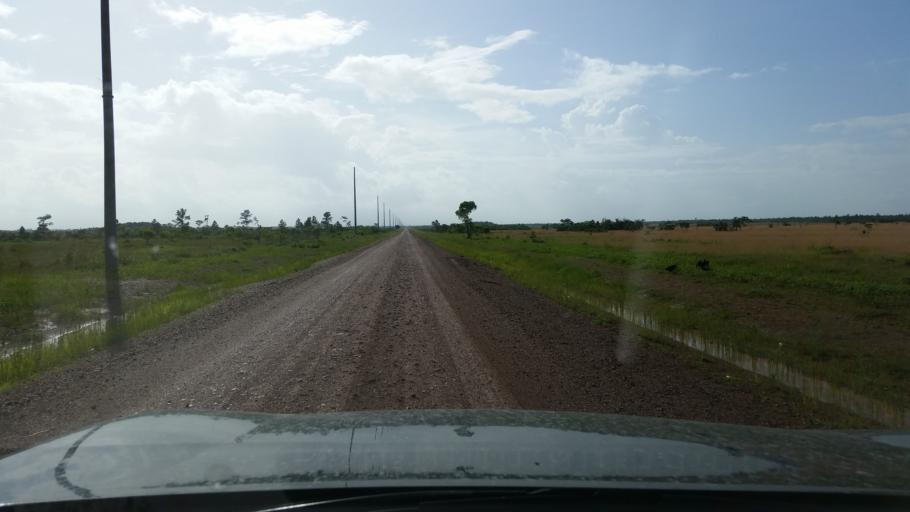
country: NI
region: Atlantico Norte (RAAN)
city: Puerto Cabezas
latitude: 14.1101
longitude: -83.6080
